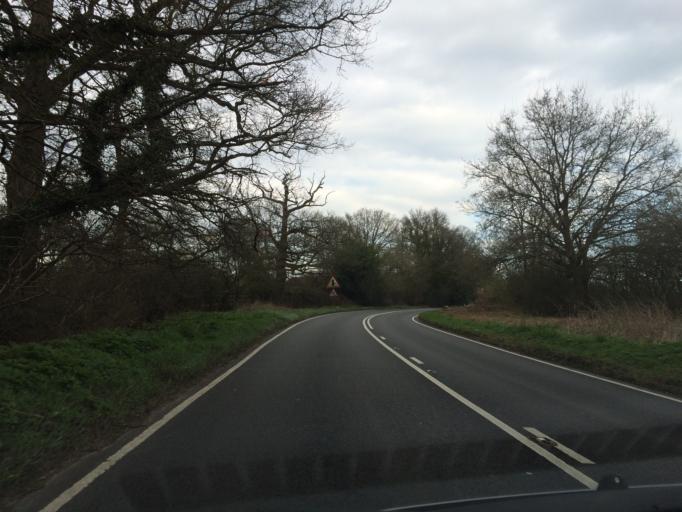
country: GB
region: England
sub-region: Surrey
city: Woking
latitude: 51.3495
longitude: -0.5728
